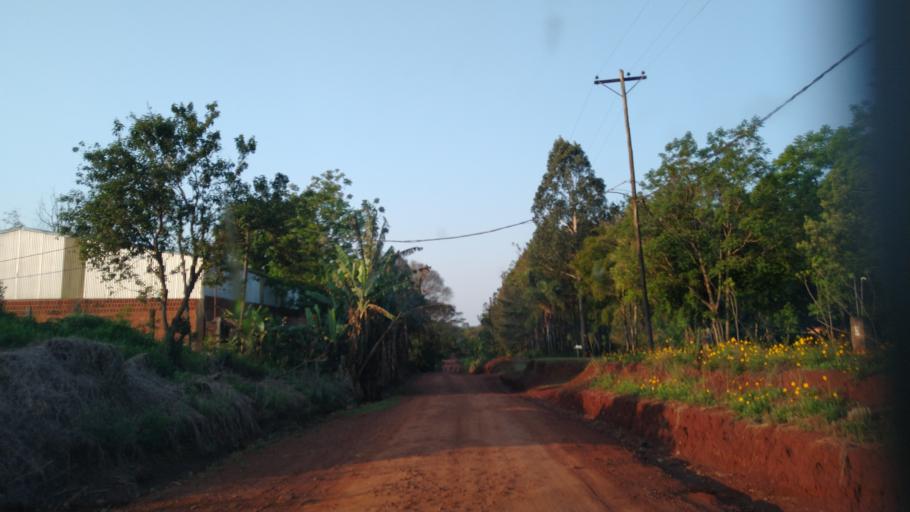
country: AR
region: Misiones
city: Jardin America
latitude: -27.0692
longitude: -55.2673
